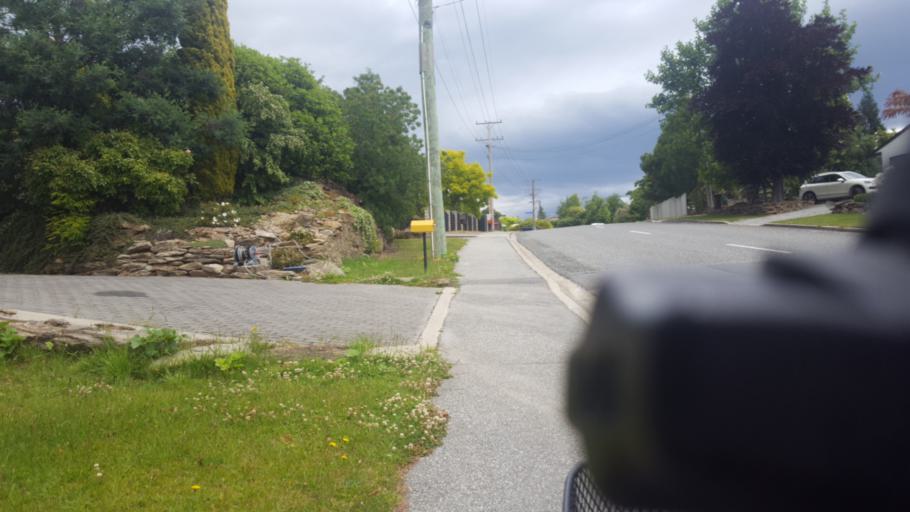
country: NZ
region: Otago
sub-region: Queenstown-Lakes District
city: Wanaka
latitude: -45.2612
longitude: 169.3796
